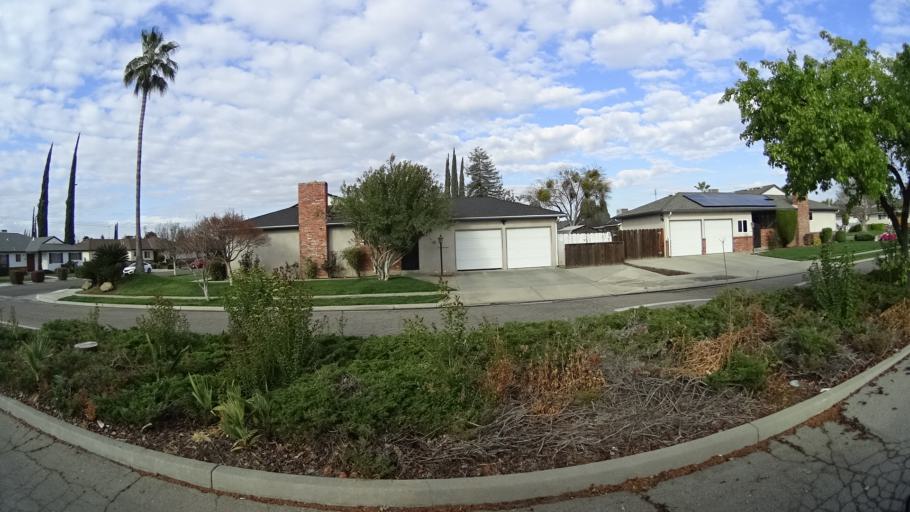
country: US
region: California
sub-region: Fresno County
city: Clovis
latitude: 36.8313
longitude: -119.7679
